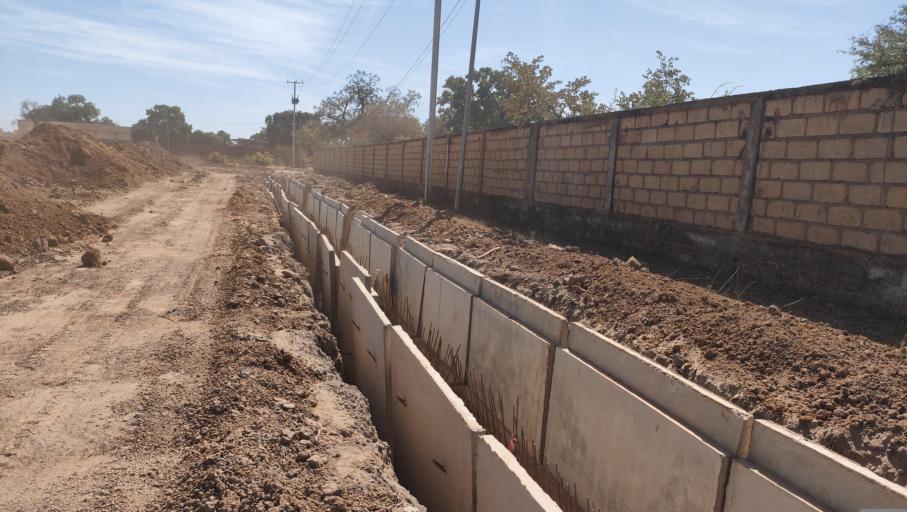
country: BF
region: Est
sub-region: Province du Gourma
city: Fada N'gourma
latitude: 12.0746
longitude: 0.3271
